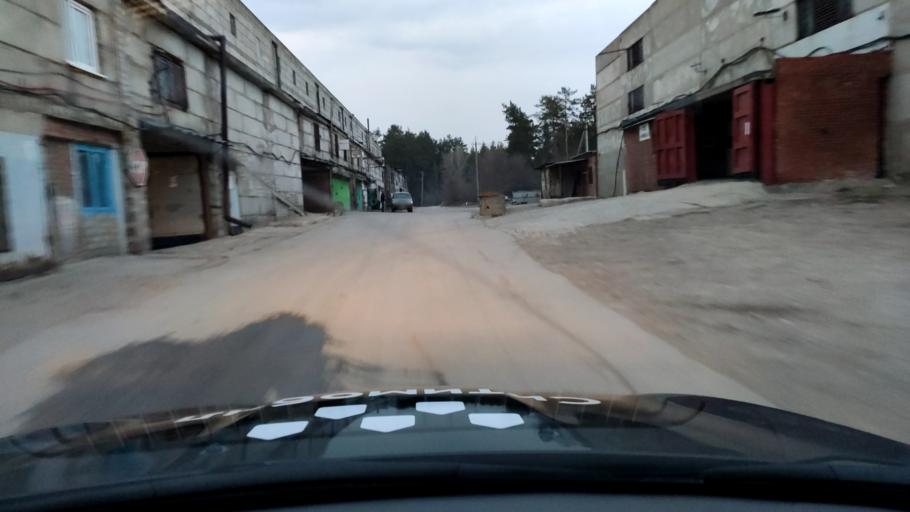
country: RU
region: Samara
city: Zhigulevsk
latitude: 53.4917
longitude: 49.4810
